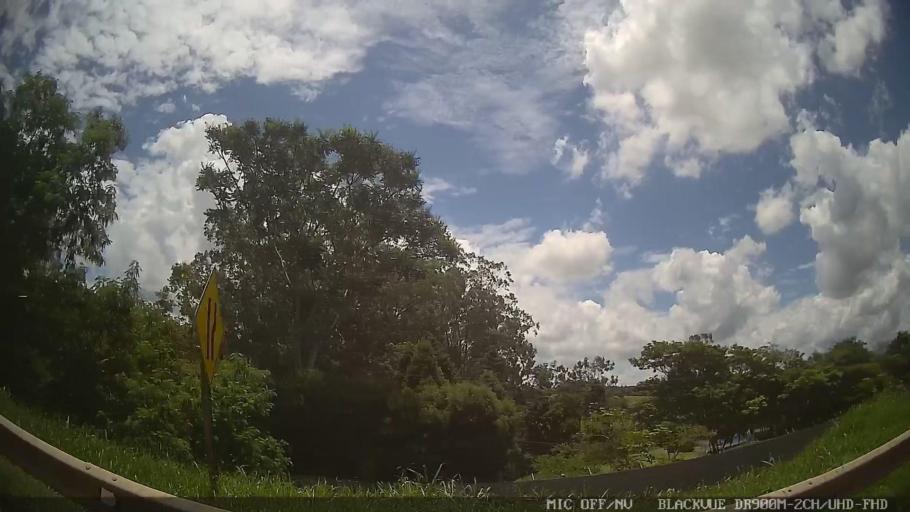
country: BR
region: Sao Paulo
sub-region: Laranjal Paulista
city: Laranjal Paulista
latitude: -23.0454
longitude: -47.8447
